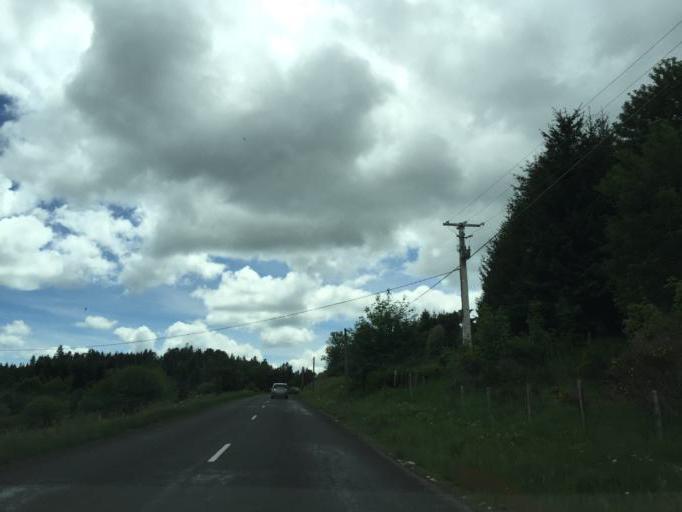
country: FR
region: Rhone-Alpes
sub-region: Departement de la Loire
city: Montbrison
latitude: 45.5424
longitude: 3.9611
